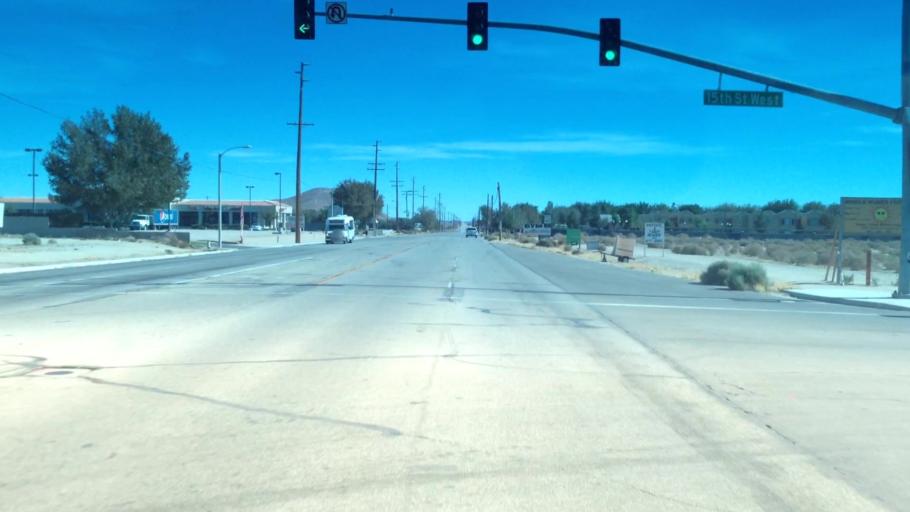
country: US
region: California
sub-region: Kern County
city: Rosamond
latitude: 34.8644
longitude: -118.1584
